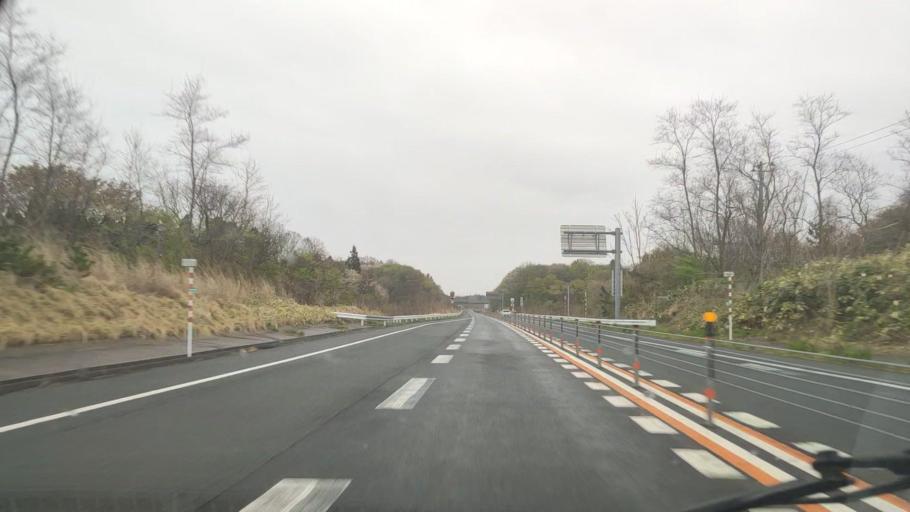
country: JP
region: Akita
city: Noshiromachi
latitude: 40.1504
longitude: 140.0213
